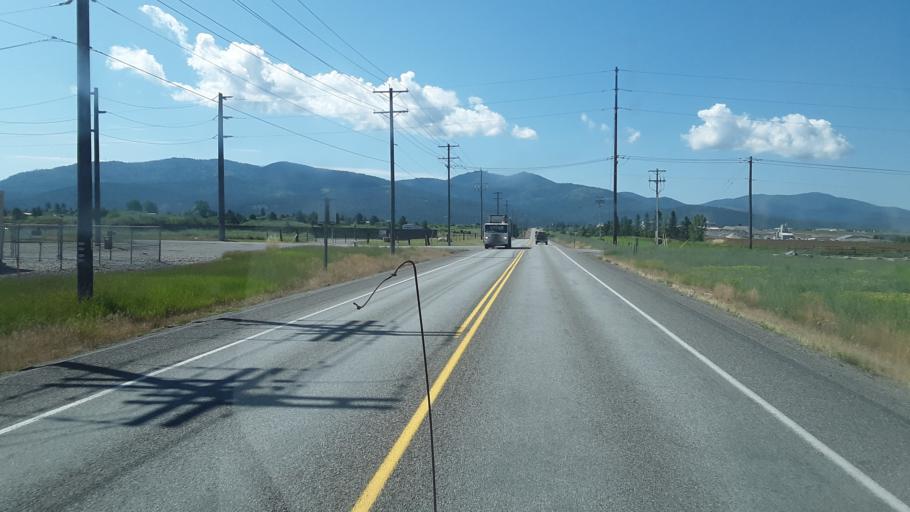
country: US
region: Idaho
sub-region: Kootenai County
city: Post Falls
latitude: 47.7319
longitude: -117.0018
